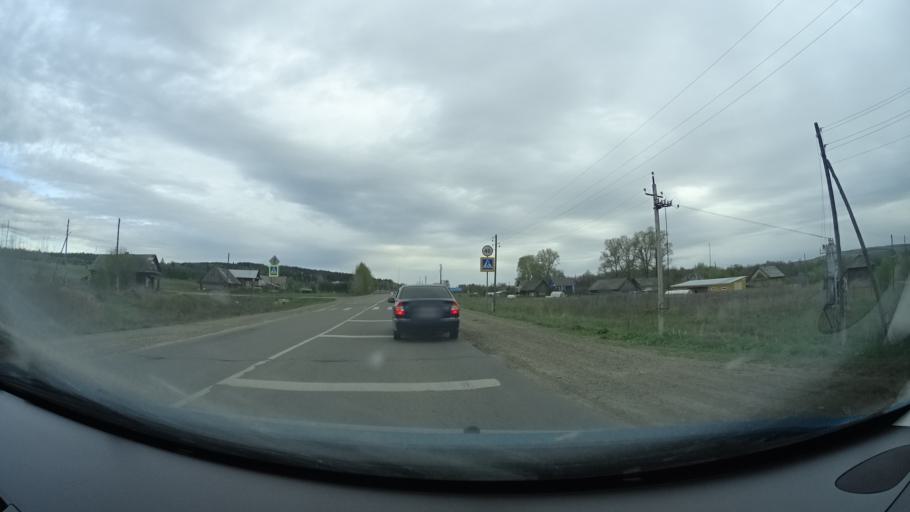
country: RU
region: Perm
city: Osa
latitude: 57.1896
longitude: 55.5911
